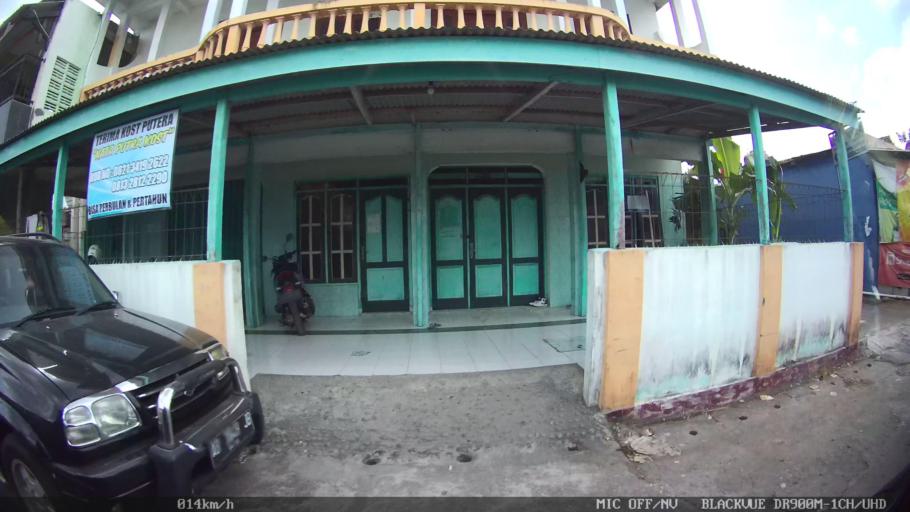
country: ID
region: Daerah Istimewa Yogyakarta
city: Gamping Lor
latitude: -7.8087
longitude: 110.3264
